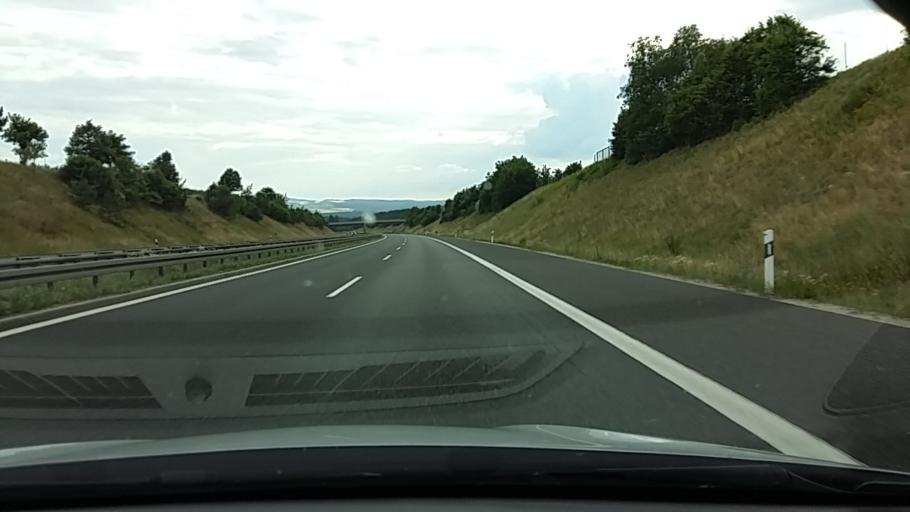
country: DE
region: Bavaria
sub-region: Upper Palatinate
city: Wernberg-Koblitz
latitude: 49.5646
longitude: 12.2093
